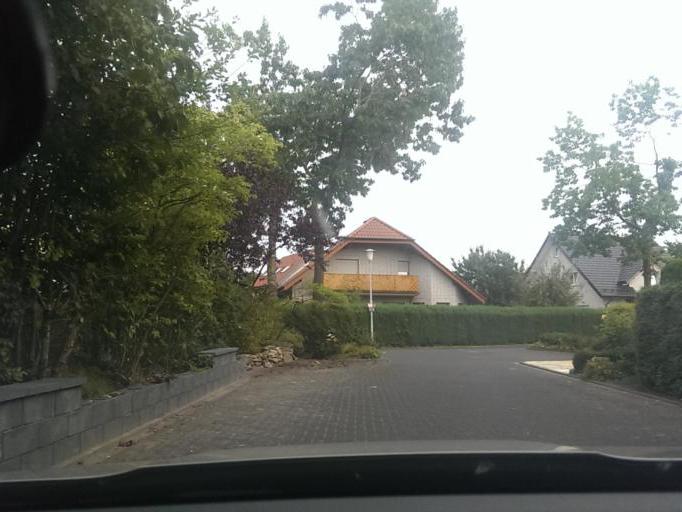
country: DE
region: North Rhine-Westphalia
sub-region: Regierungsbezirk Detmold
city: Delbruck
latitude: 51.7701
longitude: 8.5499
